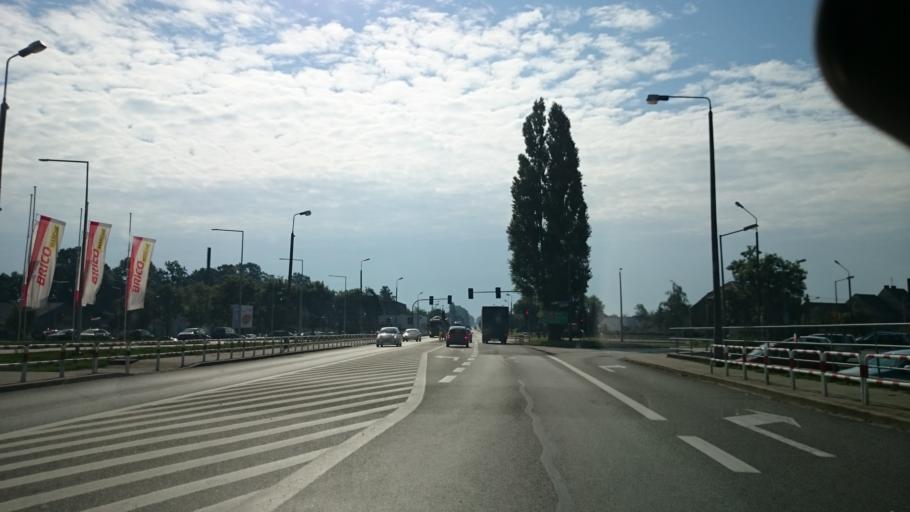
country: PL
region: Opole Voivodeship
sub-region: Powiat strzelecki
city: Strzelce Opolskie
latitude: 50.5074
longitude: 18.3108
